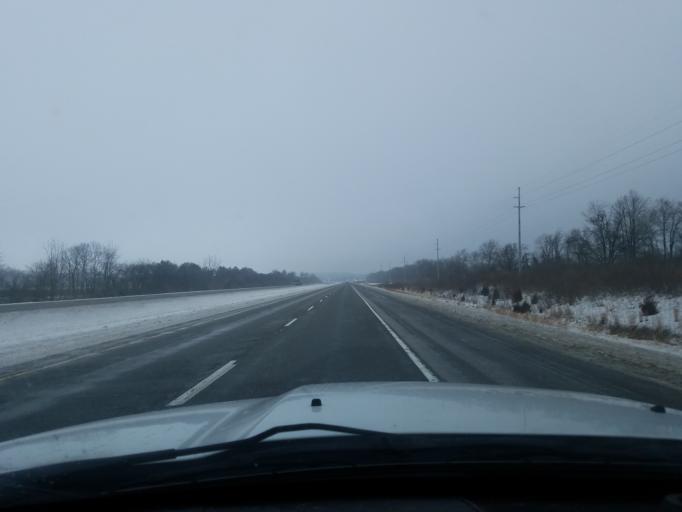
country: US
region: Indiana
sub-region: Fulton County
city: Rochester
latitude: 41.0218
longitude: -86.1763
